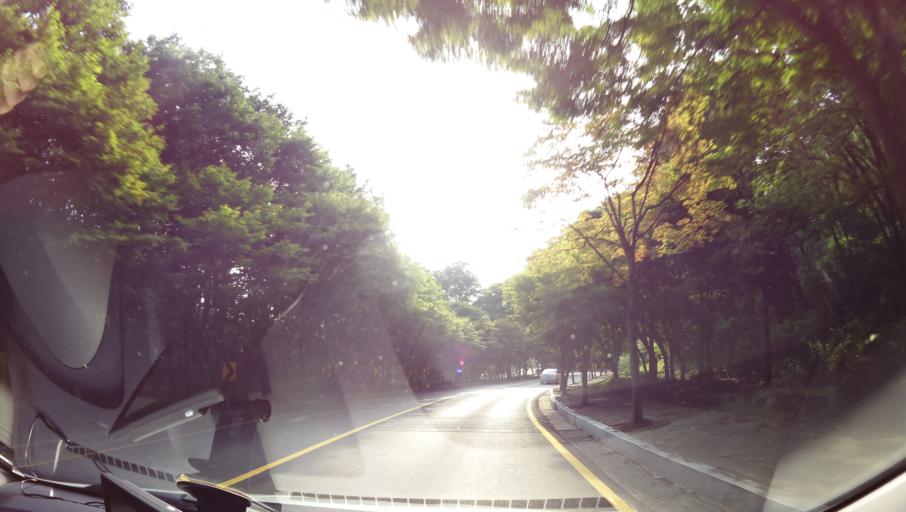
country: KR
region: Daegu
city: Daegu
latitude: 35.9853
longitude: 128.6595
